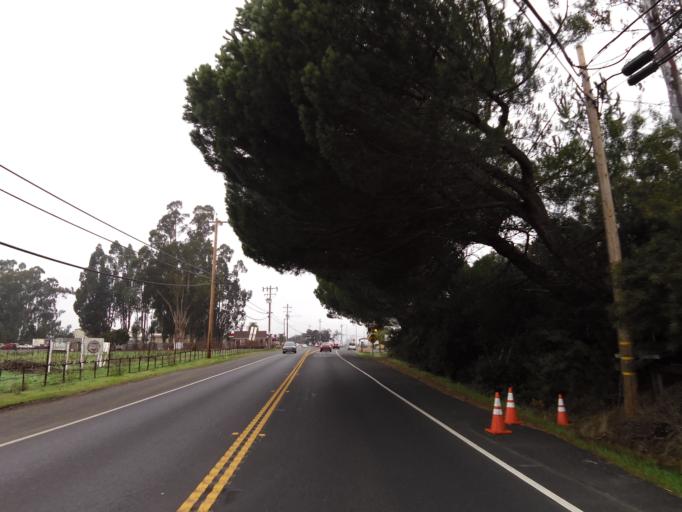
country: US
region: California
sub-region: Sonoma County
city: Temelec
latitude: 38.2339
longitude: -122.4607
